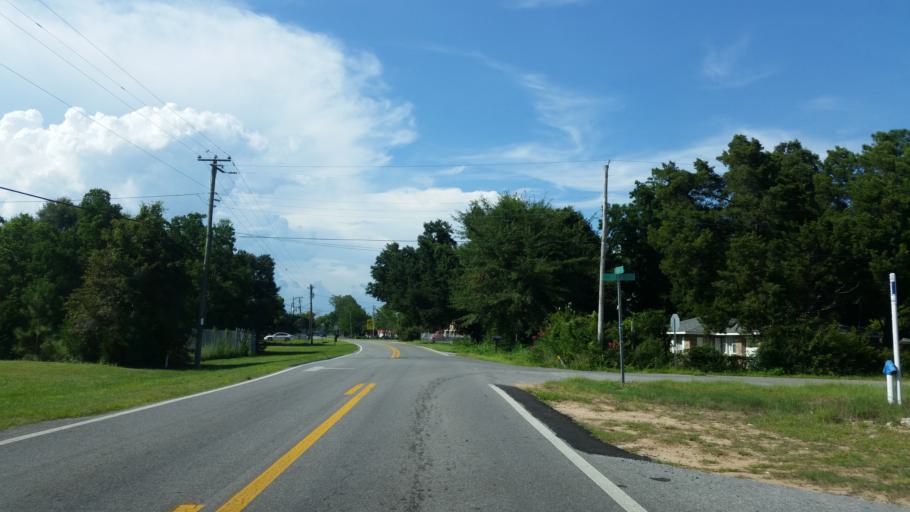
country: US
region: Florida
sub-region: Santa Rosa County
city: Pace
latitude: 30.5965
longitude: -87.1611
